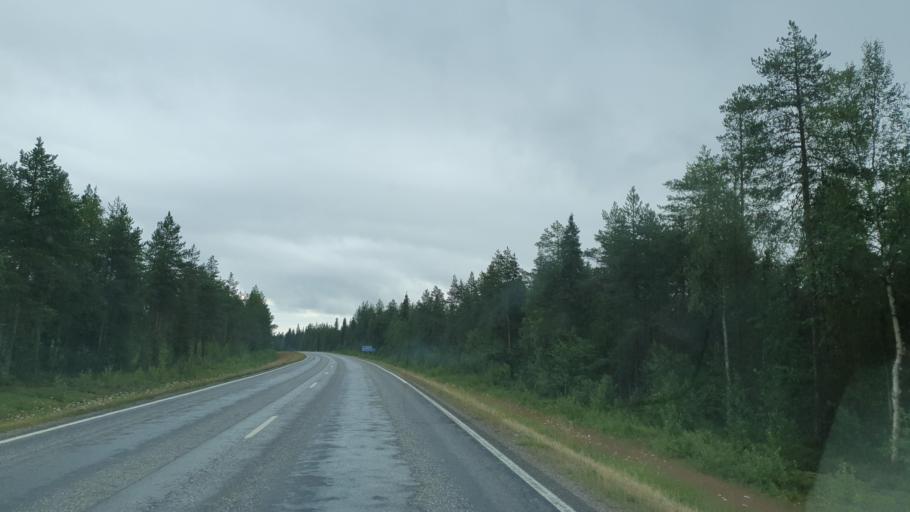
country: FI
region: Lapland
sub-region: Itae-Lappi
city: Kemijaervi
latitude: 66.8196
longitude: 27.3996
